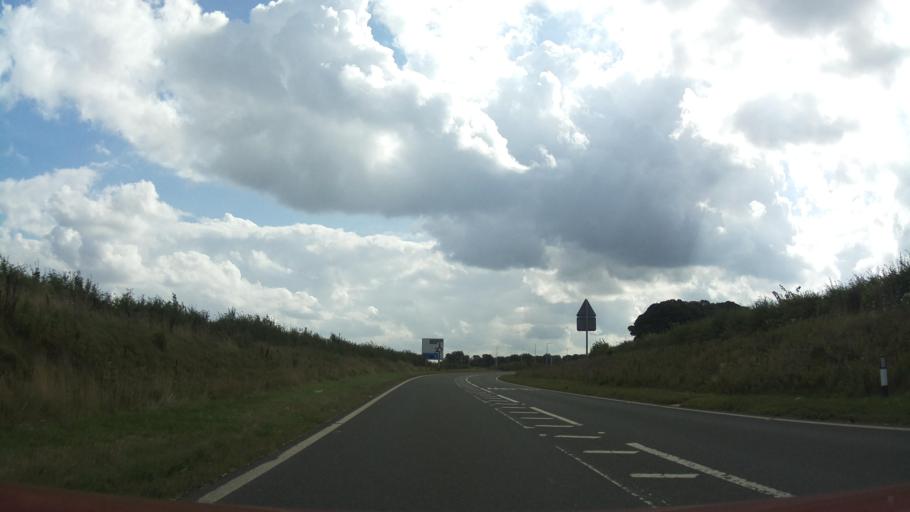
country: GB
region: England
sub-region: North Yorkshire
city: Catterick
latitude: 54.4482
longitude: -1.6705
